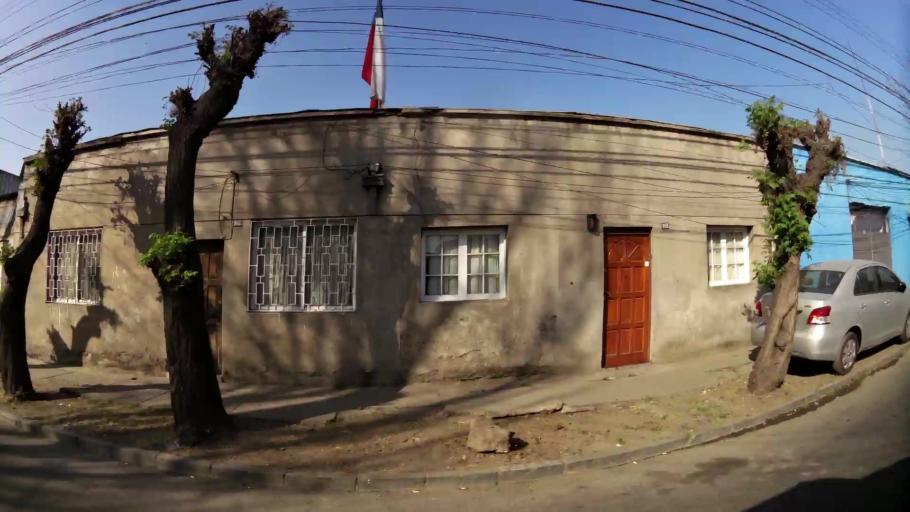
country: CL
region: Santiago Metropolitan
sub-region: Provincia de Santiago
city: Lo Prado
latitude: -33.3894
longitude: -70.6776
